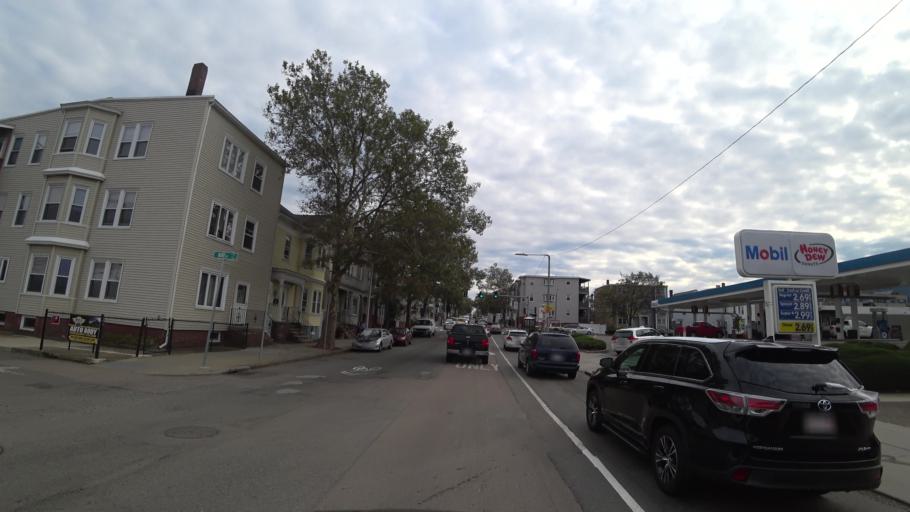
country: US
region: Massachusetts
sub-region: Suffolk County
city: Chelsea
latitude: 42.3832
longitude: -71.0393
